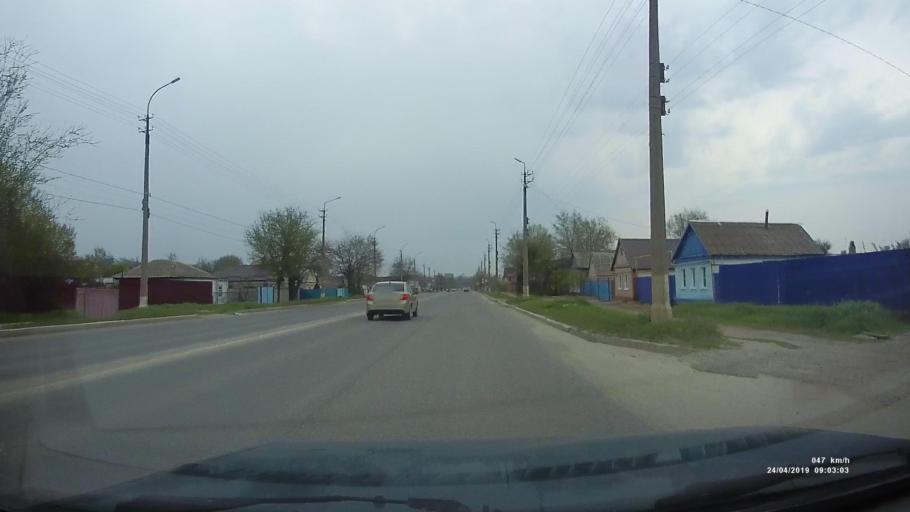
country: RU
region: Kalmykiya
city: Elista
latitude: 46.3117
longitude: 44.2348
